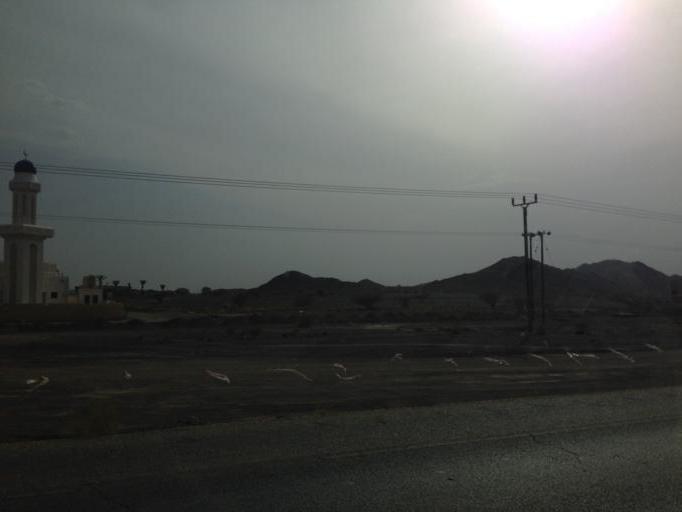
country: OM
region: Ash Sharqiyah
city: Al Qabil
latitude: 22.6354
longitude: 58.6437
